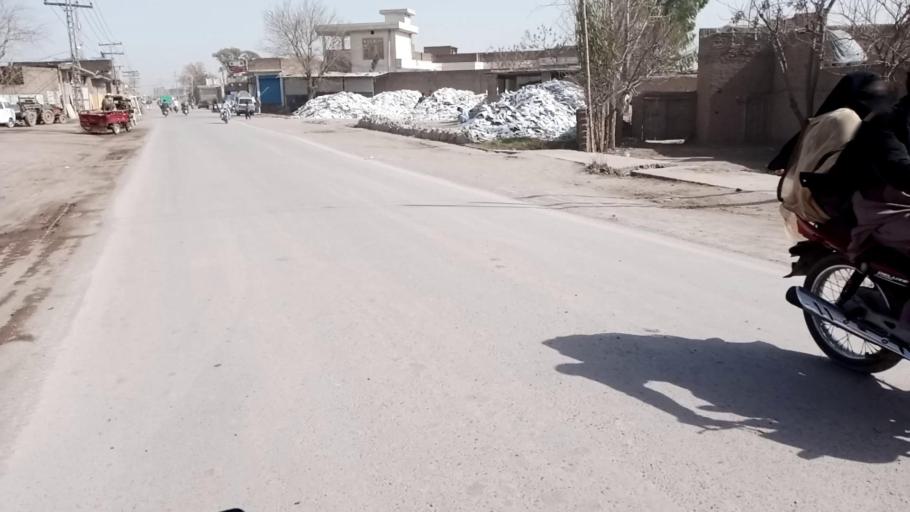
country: PK
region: Khyber Pakhtunkhwa
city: Peshawar
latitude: 34.0020
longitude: 71.6377
